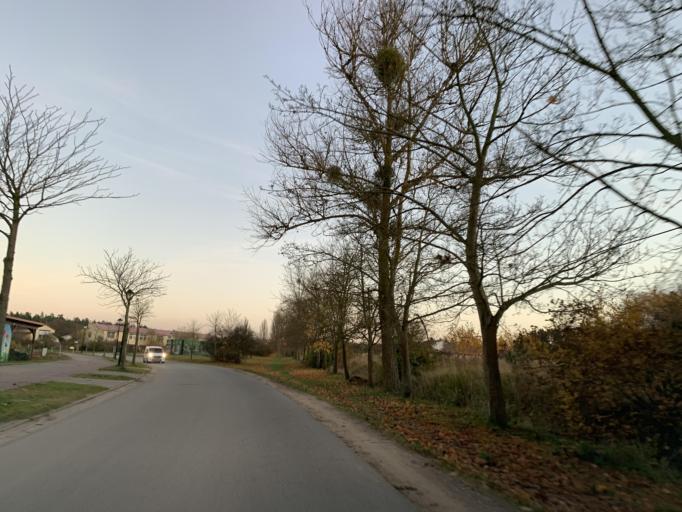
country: DE
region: Mecklenburg-Vorpommern
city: Loitz
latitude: 53.3294
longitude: 13.4361
